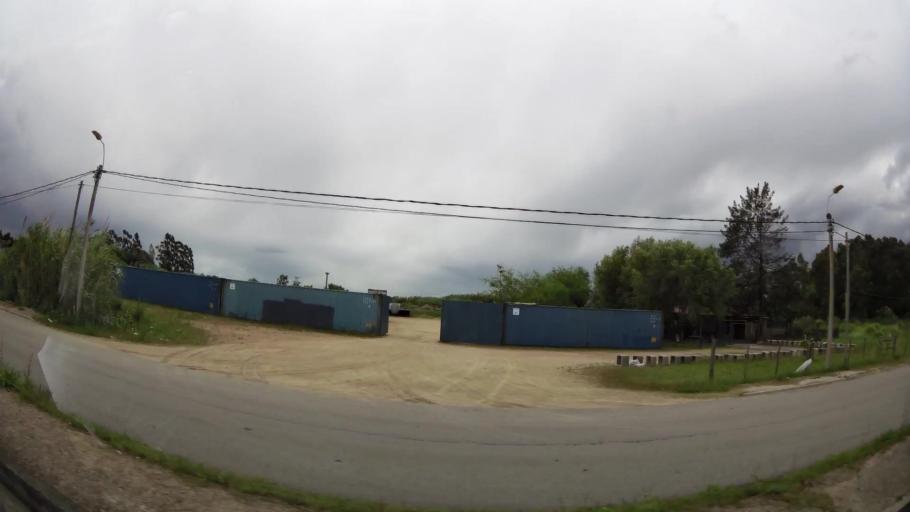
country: UY
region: Canelones
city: Toledo
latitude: -34.7961
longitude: -56.1434
